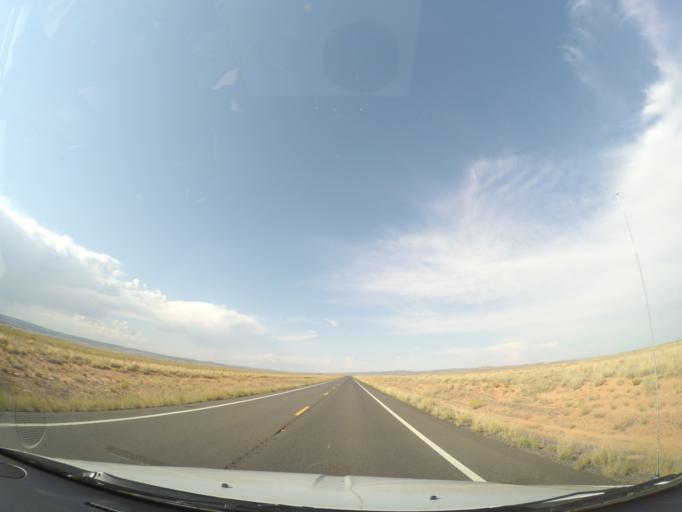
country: US
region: Arizona
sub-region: Coconino County
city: Tuba City
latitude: 36.3832
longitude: -111.4194
